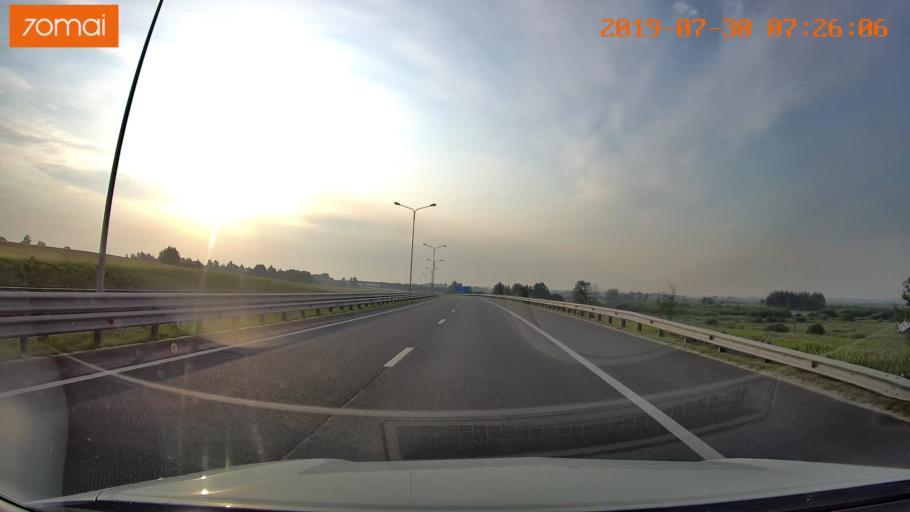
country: RU
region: Kaliningrad
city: Gvardeysk
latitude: 54.6838
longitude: 20.8522
